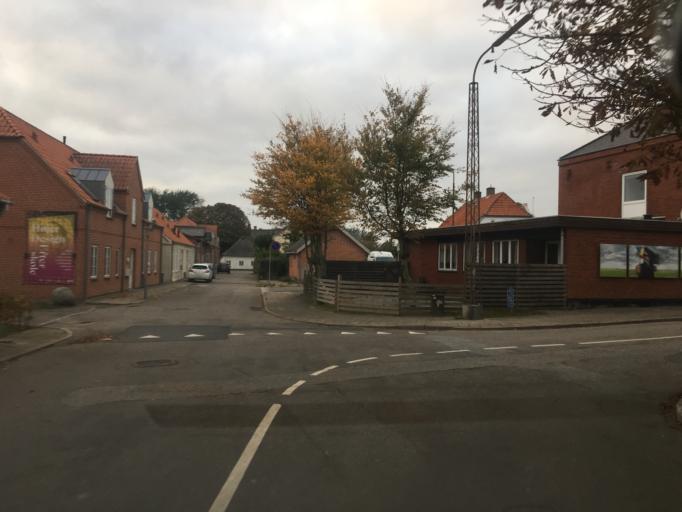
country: DE
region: Schleswig-Holstein
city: Rodenas
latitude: 54.9626
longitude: 8.6945
